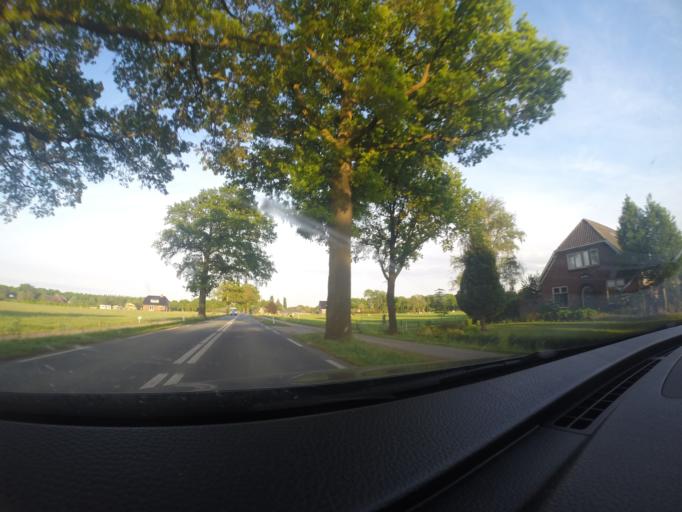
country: NL
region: Gelderland
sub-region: Gemeente Voorst
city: Twello
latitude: 52.1904
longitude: 6.0847
